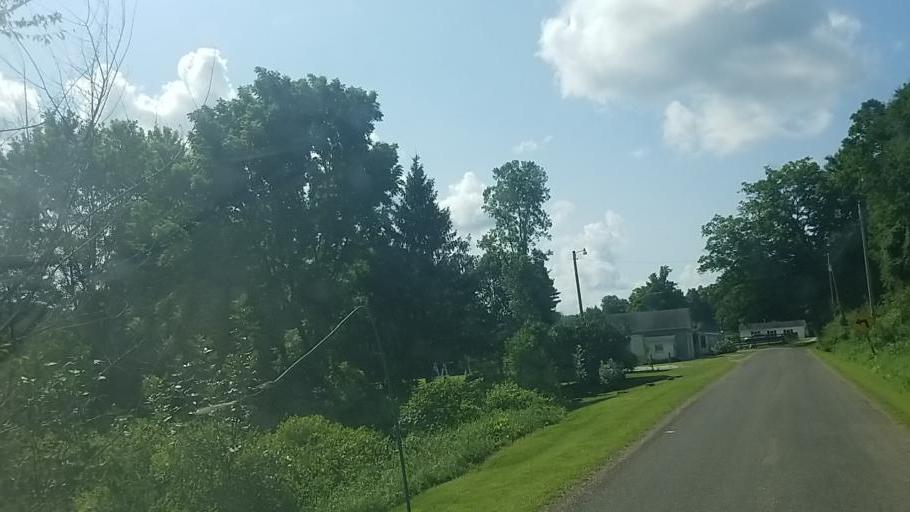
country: US
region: Ohio
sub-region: Ashland County
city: Ashland
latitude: 40.7490
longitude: -82.3000
